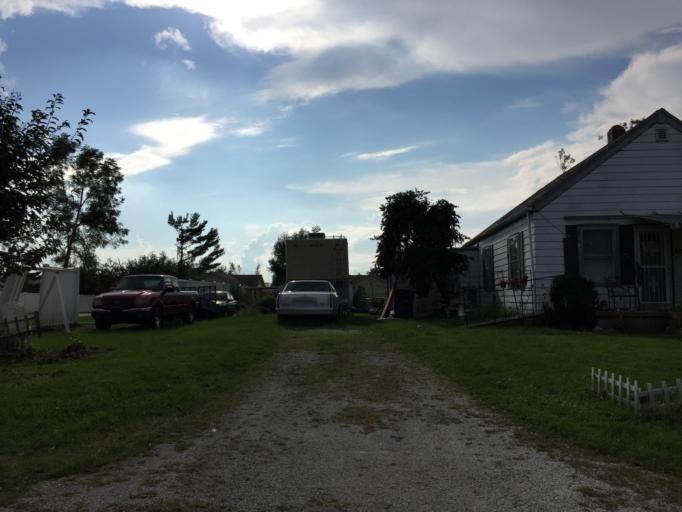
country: US
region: Indiana
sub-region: Howard County
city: Kokomo
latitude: 40.4686
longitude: -86.1138
